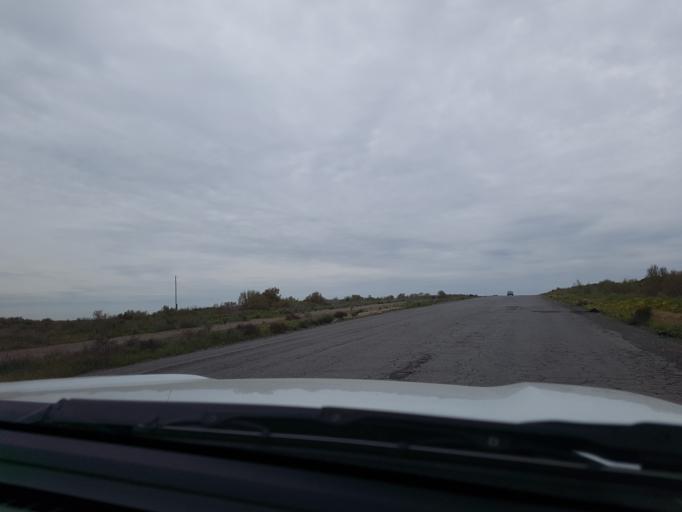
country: TM
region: Mary
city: Bayramaly
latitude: 37.8863
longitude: 62.6145
